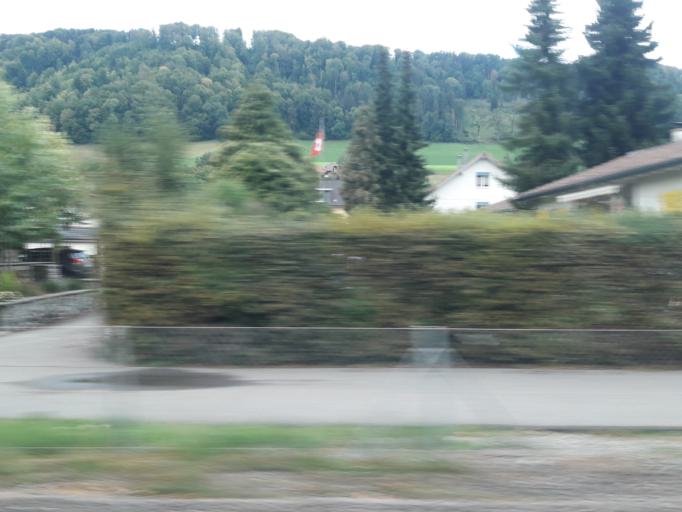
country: CH
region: Bern
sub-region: Bern-Mittelland District
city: Toffen
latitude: 46.8555
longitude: 7.4967
